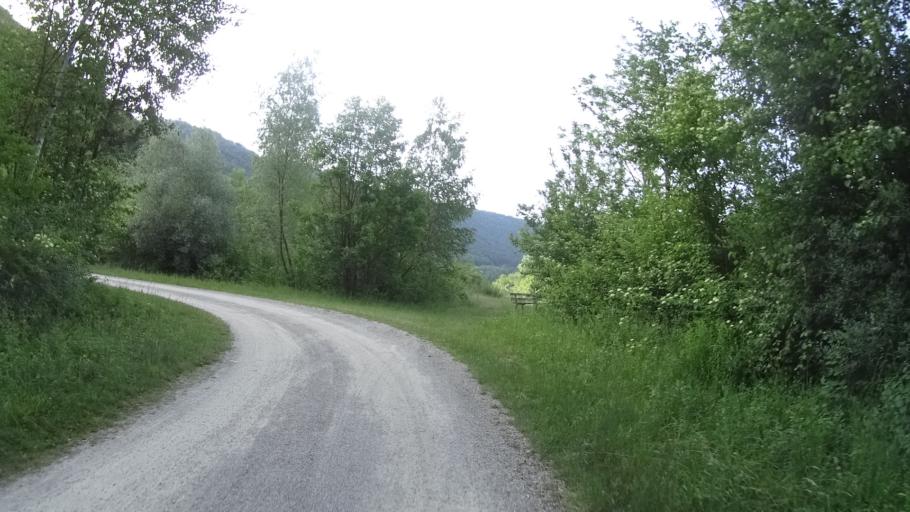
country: DE
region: Bavaria
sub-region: Lower Bavaria
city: Riedenburg
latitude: 48.9909
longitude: 11.6889
